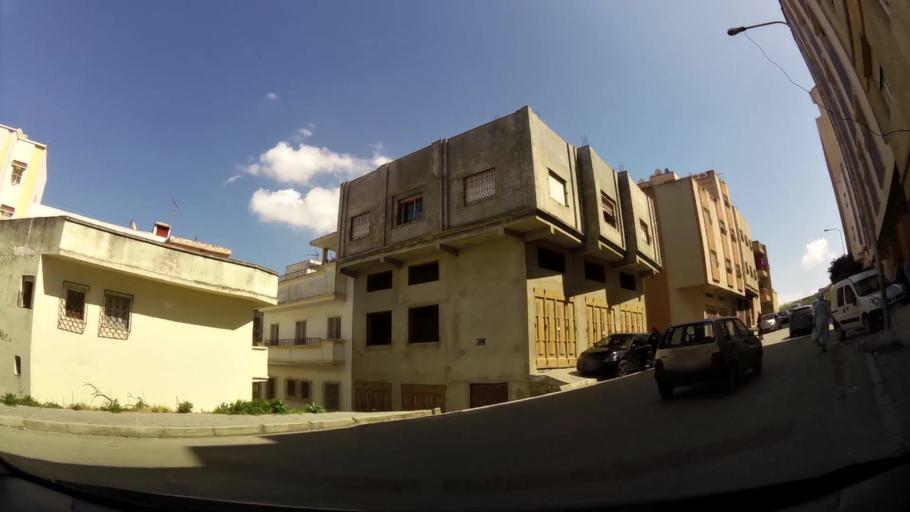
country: MA
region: Tanger-Tetouan
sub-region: Tanger-Assilah
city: Tangier
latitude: 35.7513
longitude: -5.8162
